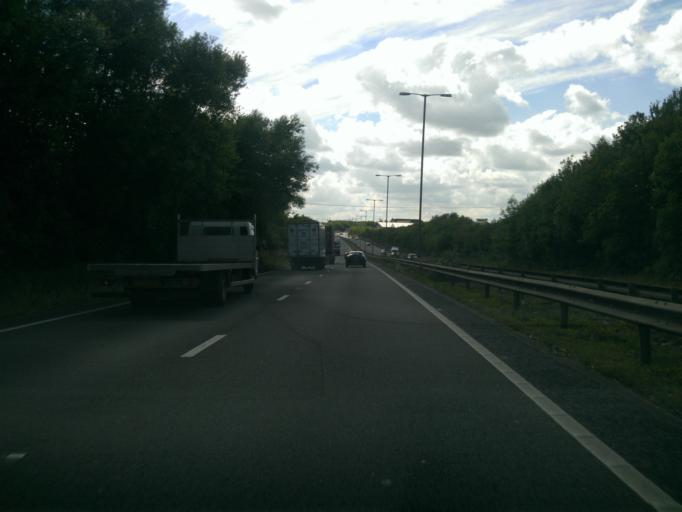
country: GB
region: England
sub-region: Northamptonshire
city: Burton Latimer
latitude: 52.3735
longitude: -0.6979
